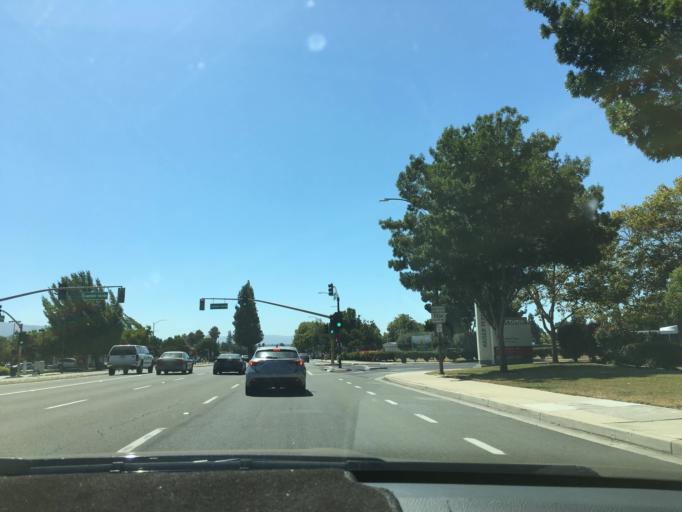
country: US
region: California
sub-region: Santa Clara County
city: Seven Trees
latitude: 37.2372
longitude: -121.8004
